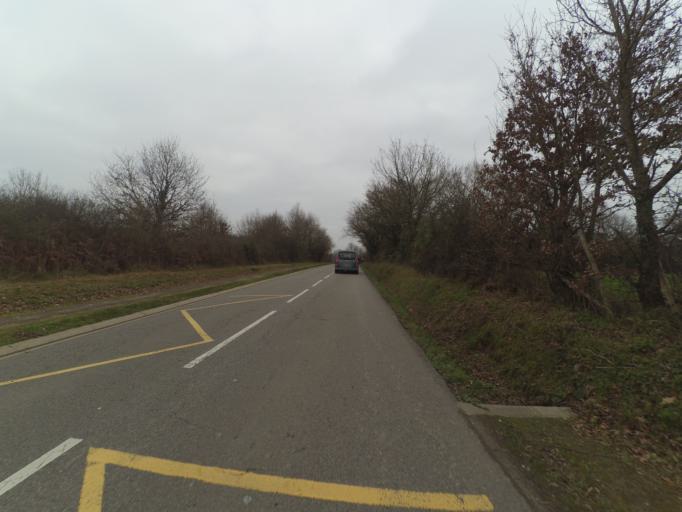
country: FR
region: Pays de la Loire
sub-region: Departement de la Loire-Atlantique
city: Saint-Herblain
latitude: 47.2204
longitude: -1.6590
